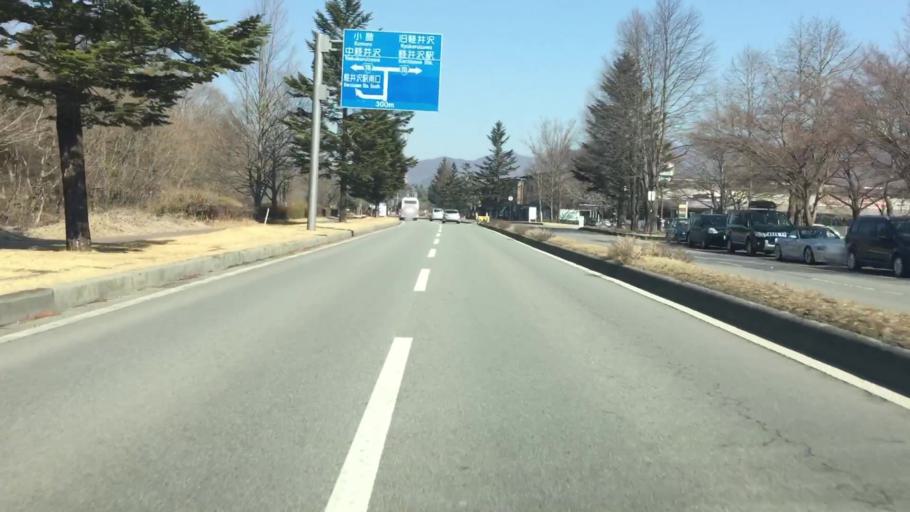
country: JP
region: Nagano
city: Saku
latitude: 36.3384
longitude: 138.6310
